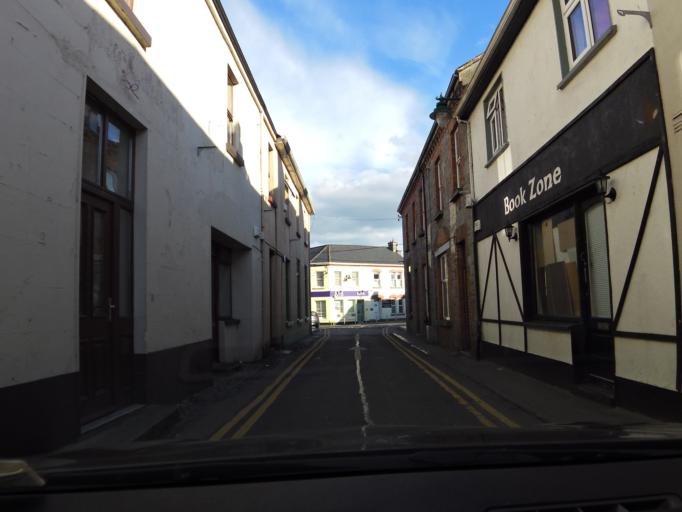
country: IE
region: Connaught
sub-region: County Galway
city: Athenry
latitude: 53.2993
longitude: -8.7464
